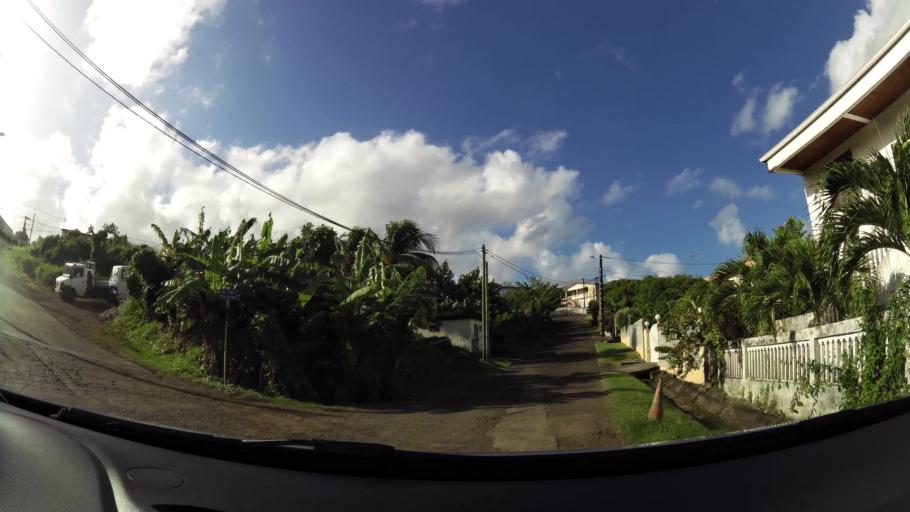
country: MQ
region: Martinique
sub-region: Martinique
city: Le Francois
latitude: 14.6144
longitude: -60.9094
